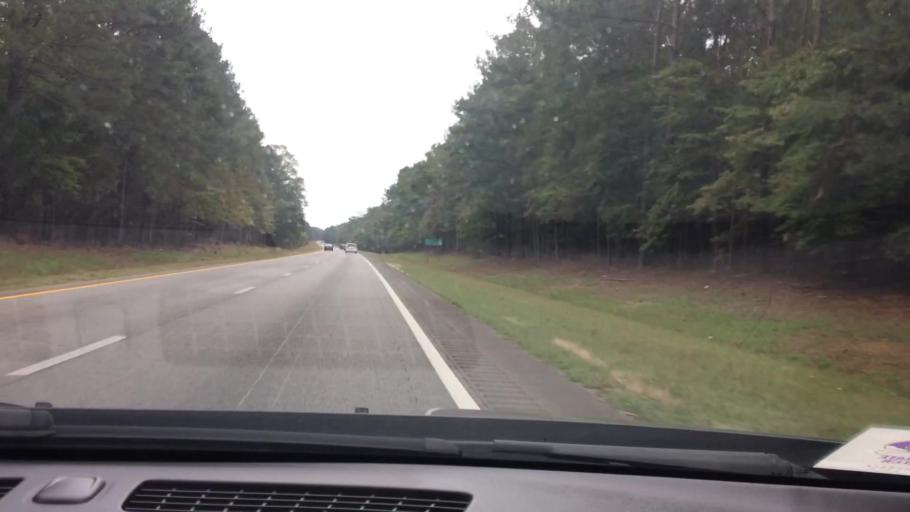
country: US
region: North Carolina
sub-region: Wake County
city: Zebulon
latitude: 35.7955
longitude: -78.1769
